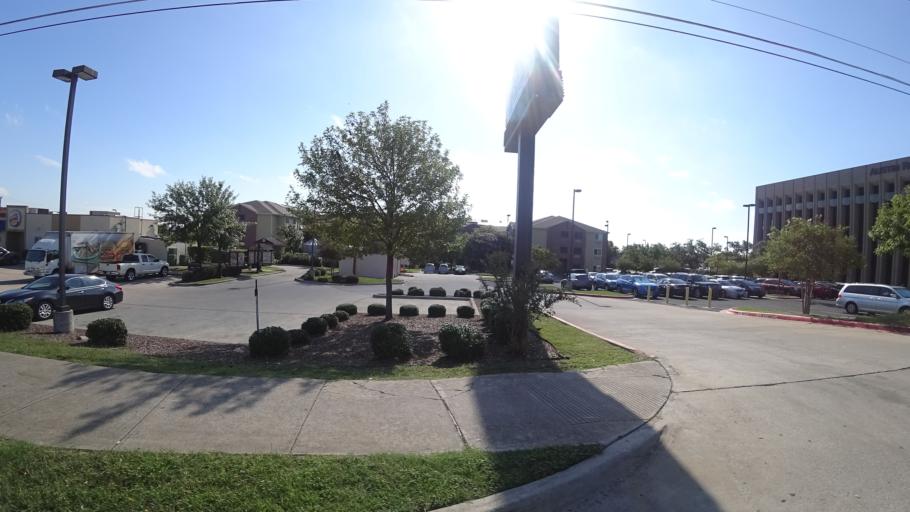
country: US
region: Texas
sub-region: Travis County
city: Austin
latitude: 30.3318
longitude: -97.7041
